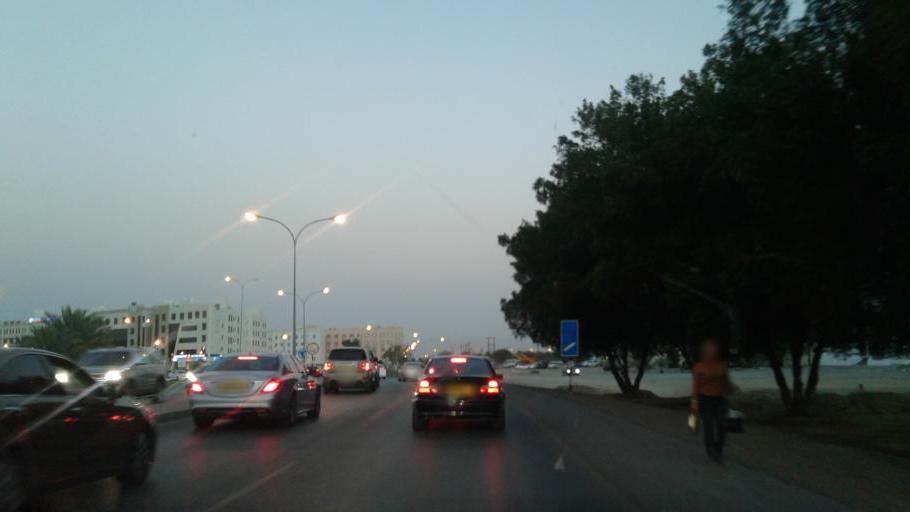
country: OM
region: Muhafazat Masqat
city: As Sib al Jadidah
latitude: 23.6110
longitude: 58.2400
